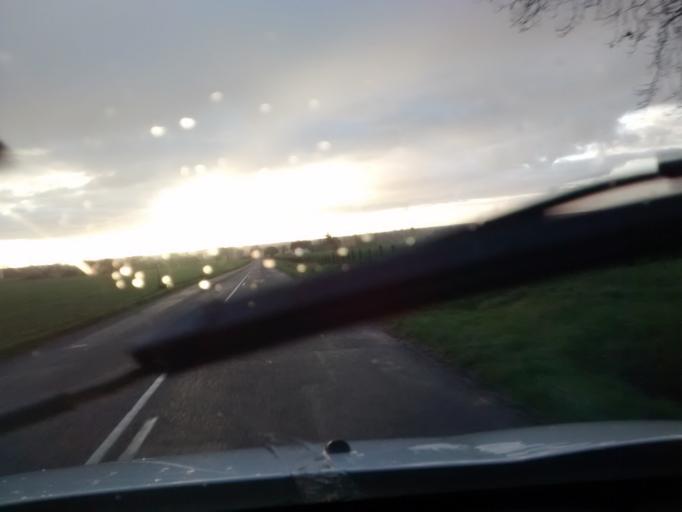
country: FR
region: Brittany
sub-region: Departement d'Ille-et-Vilaine
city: Bais
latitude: 47.9802
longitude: -1.2762
